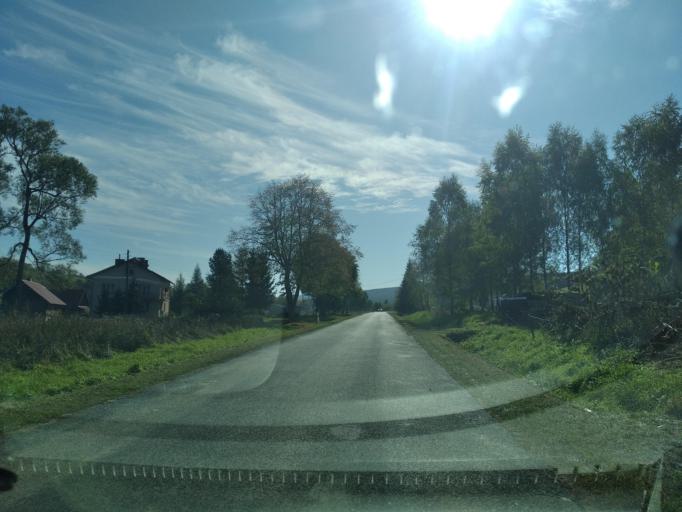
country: PL
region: Subcarpathian Voivodeship
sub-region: Powiat sanocki
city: Komancza
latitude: 49.4063
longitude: 21.9784
